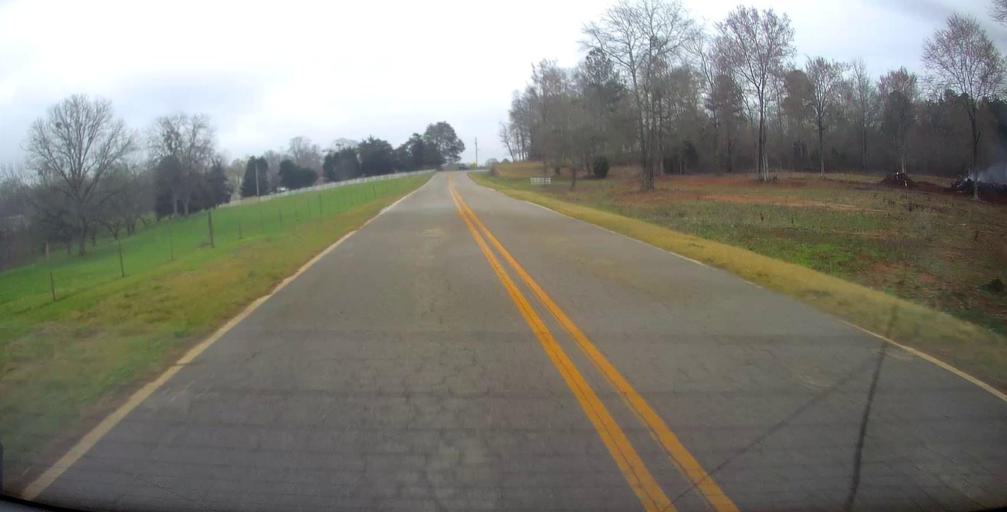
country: US
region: Georgia
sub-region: Monroe County
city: Forsyth
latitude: 33.0465
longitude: -83.8758
